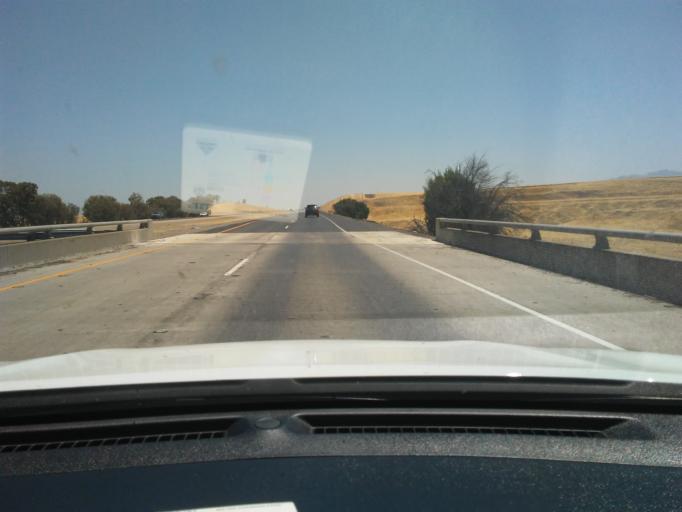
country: US
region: California
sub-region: San Joaquin County
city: Tracy
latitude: 37.6699
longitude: -121.4538
